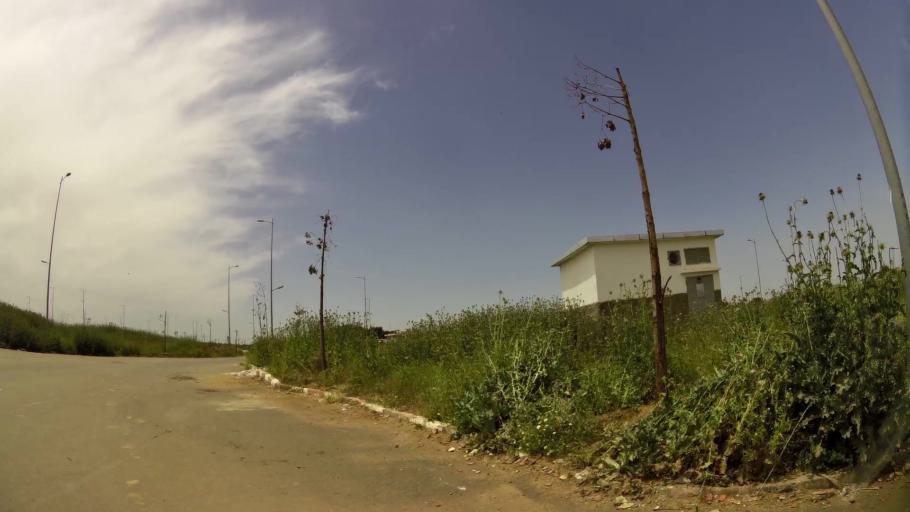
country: MA
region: Rabat-Sale-Zemmour-Zaer
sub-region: Khemisset
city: Khemisset
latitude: 33.8198
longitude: -6.0871
